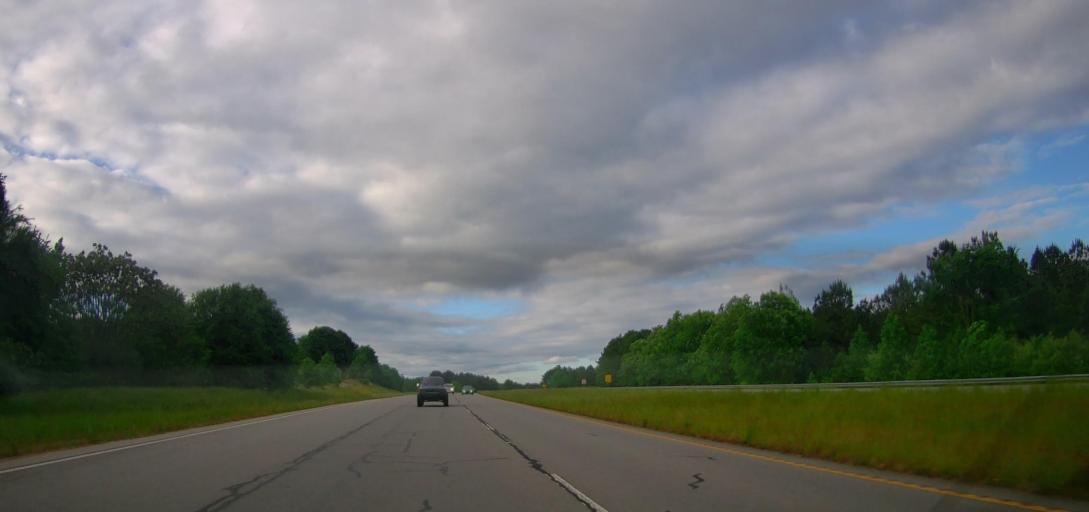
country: US
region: Georgia
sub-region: Oconee County
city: Watkinsville
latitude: 33.8652
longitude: -83.4244
